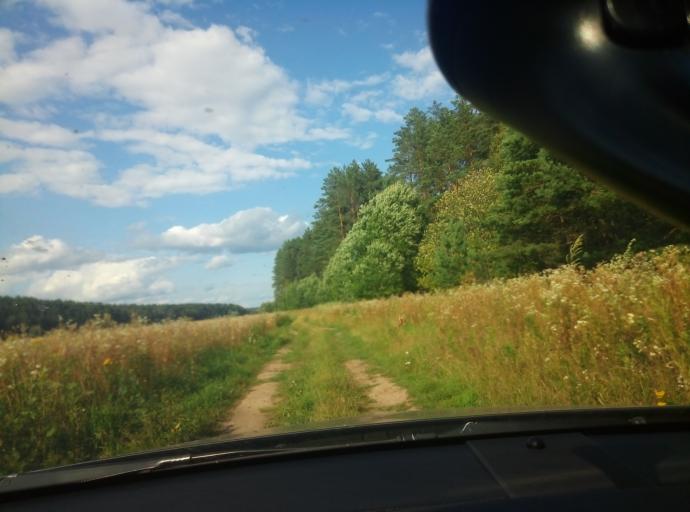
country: RU
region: Kaluga
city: Yukhnov
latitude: 54.7299
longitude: 35.1183
